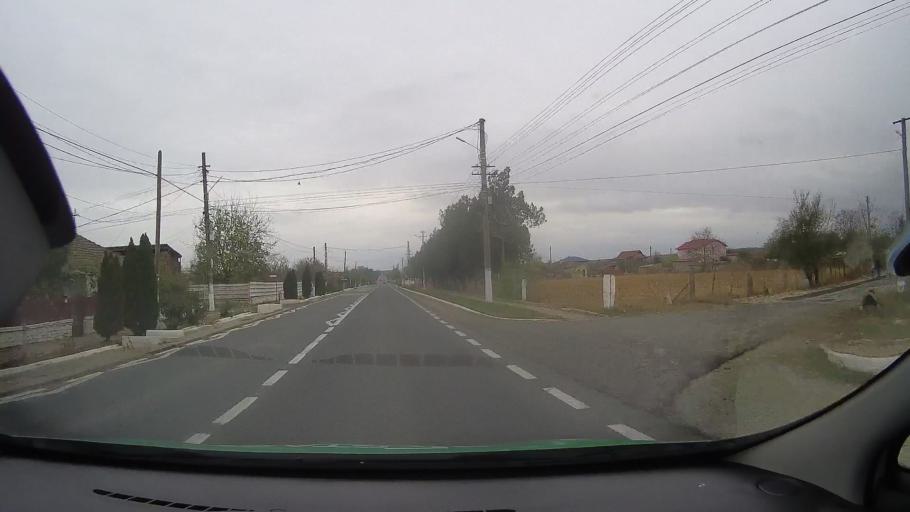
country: RO
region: Constanta
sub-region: Comuna Nicolae Balcescu
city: Nicolae Balcescu
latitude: 44.3891
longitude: 28.3729
